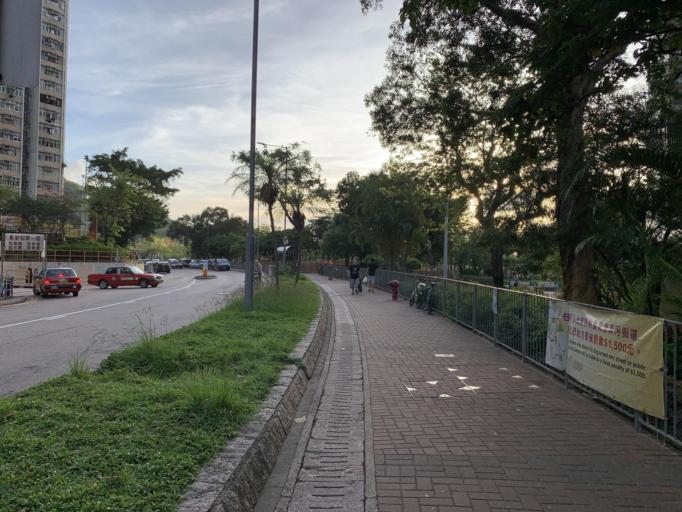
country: HK
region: Tsuen Wan
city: Tsuen Wan
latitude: 22.3623
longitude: 114.1012
